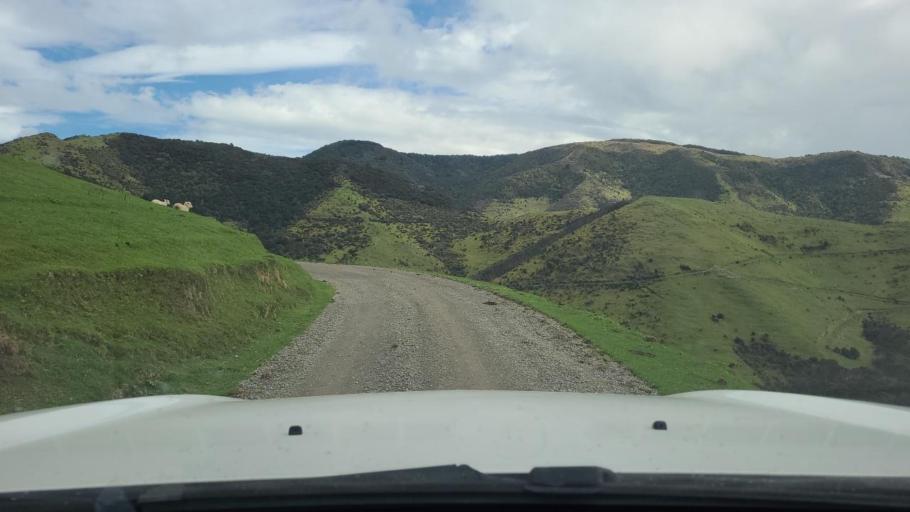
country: NZ
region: Wellington
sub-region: South Wairarapa District
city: Waipawa
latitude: -41.3658
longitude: 175.3849
